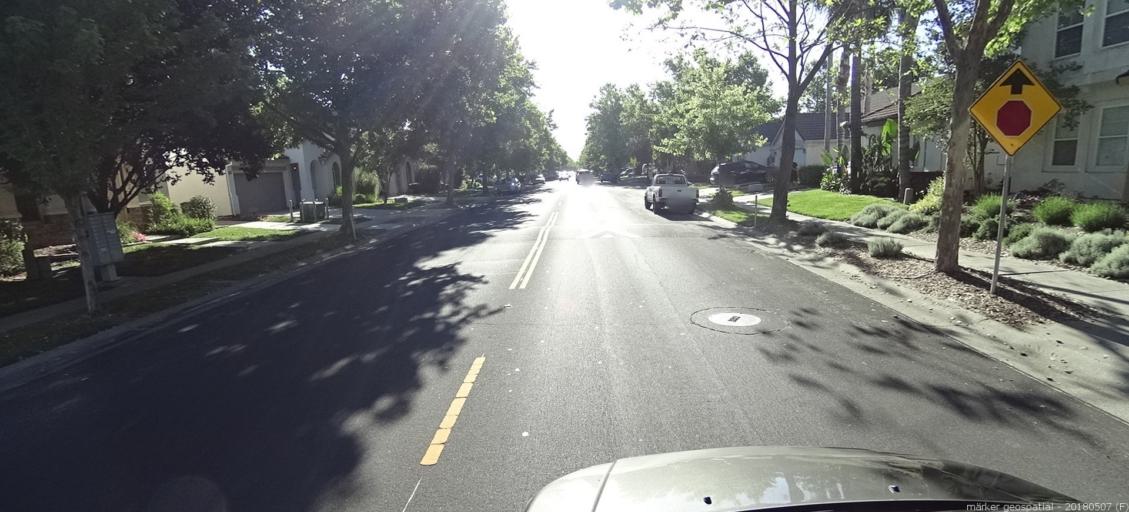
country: US
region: California
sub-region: Sacramento County
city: Rio Linda
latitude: 38.6595
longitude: -121.5055
